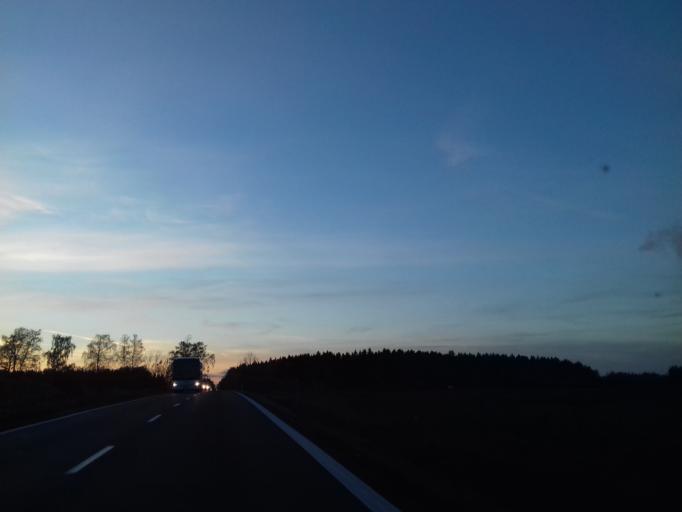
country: CZ
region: Vysocina
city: Chotebor
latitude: 49.6751
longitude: 15.7527
